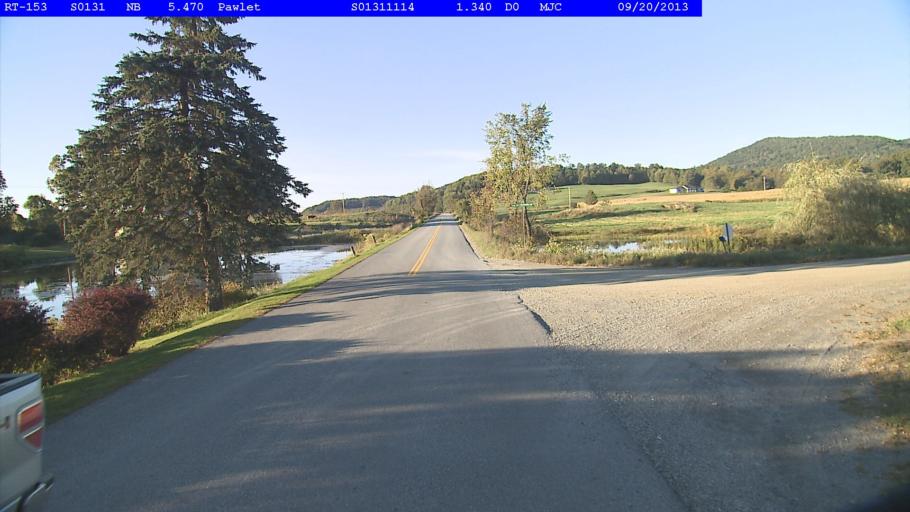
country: US
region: New York
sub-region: Washington County
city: Granville
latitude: 43.3333
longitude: -73.2434
